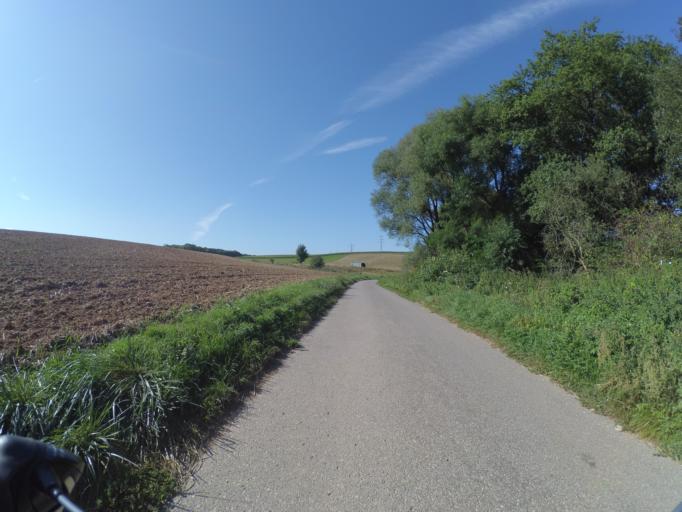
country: DE
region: Rheinland-Pfalz
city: Hetzerath
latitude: 49.8809
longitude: 6.8304
